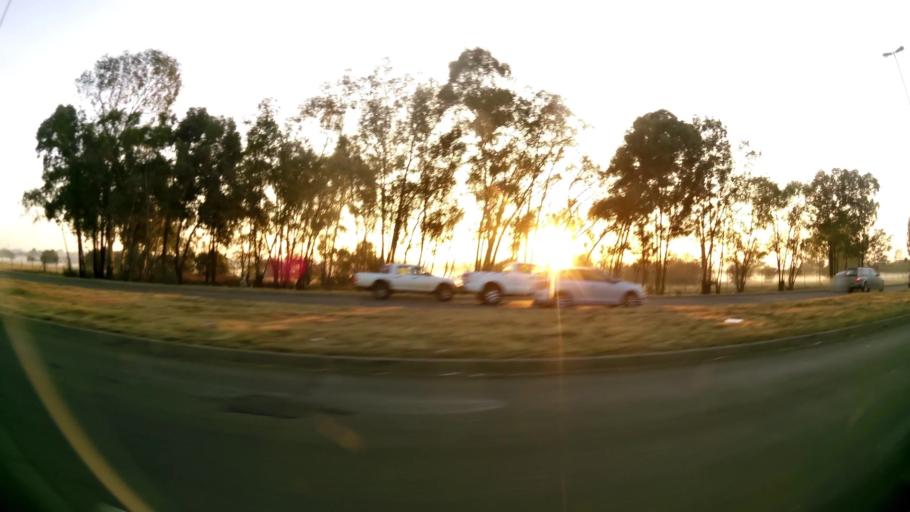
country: ZA
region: Orange Free State
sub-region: Mangaung Metropolitan Municipality
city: Bloemfontein
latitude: -29.1008
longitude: 26.1829
